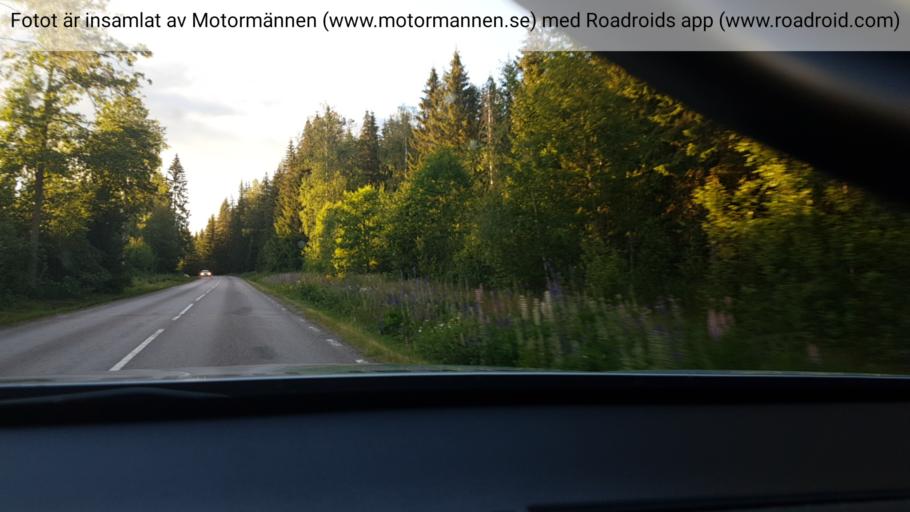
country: SE
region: Vaermland
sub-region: Torsby Kommun
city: Torsby
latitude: 60.0933
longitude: 13.0857
